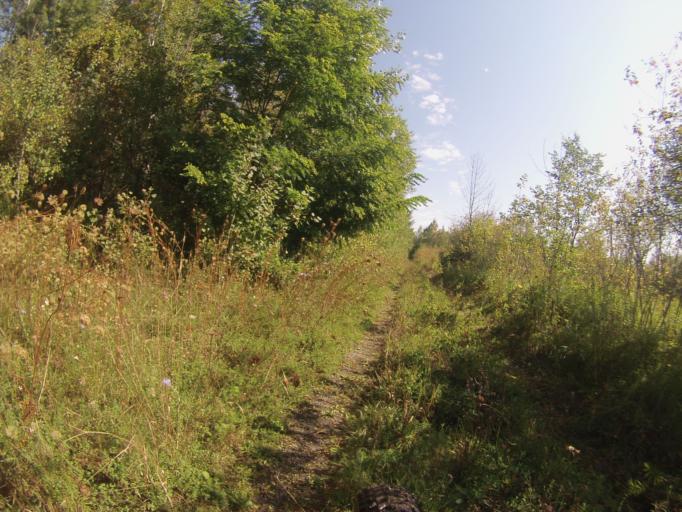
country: CA
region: Ontario
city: Ottawa
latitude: 45.3708
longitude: -75.6431
